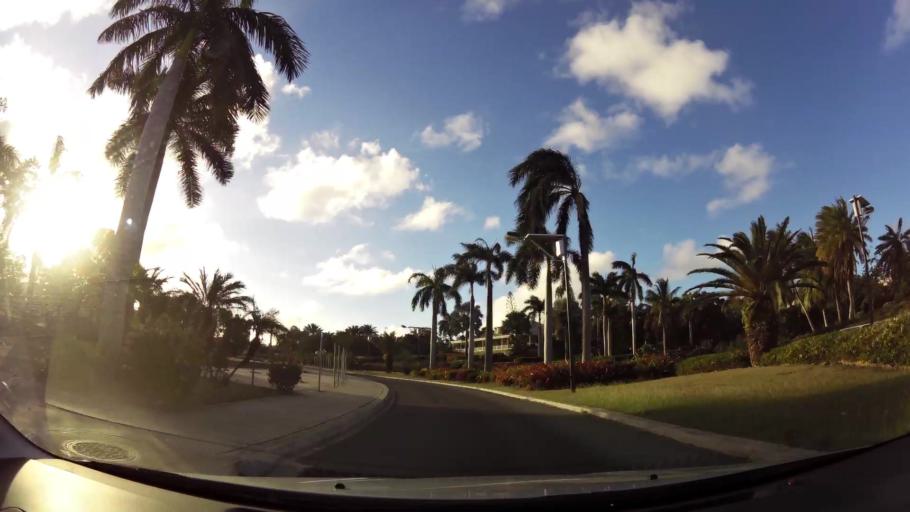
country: AG
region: Saint George
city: Piggotts
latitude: 17.1418
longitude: -61.7942
